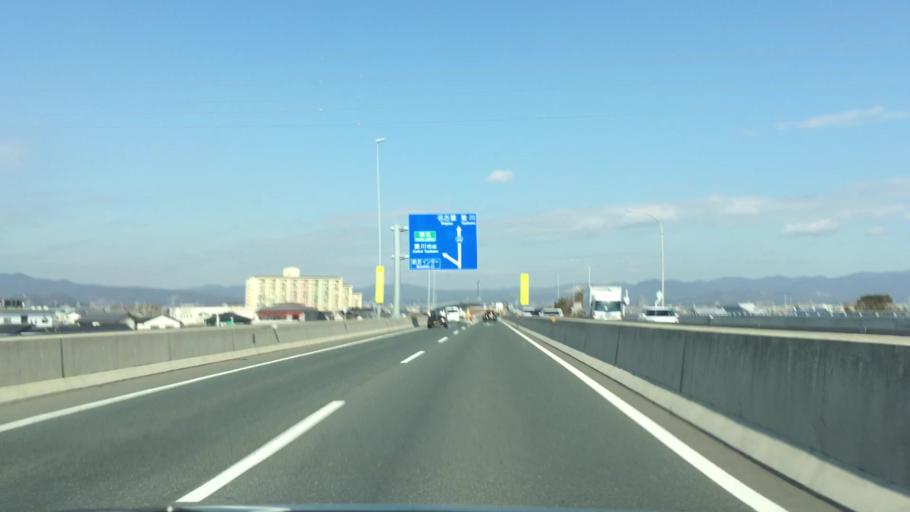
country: JP
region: Aichi
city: Kozakai-cho
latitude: 34.7793
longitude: 137.3326
